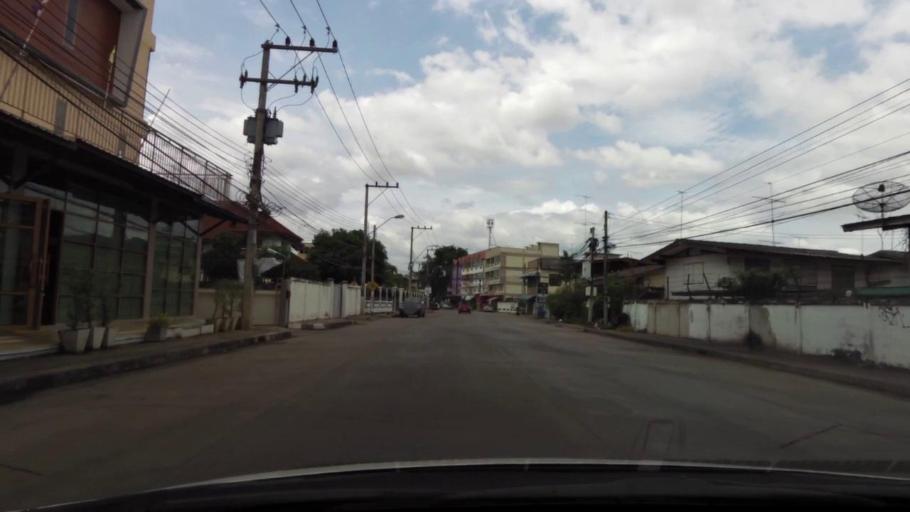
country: TH
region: Ratchaburi
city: Ratchaburi
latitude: 13.5357
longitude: 99.8279
